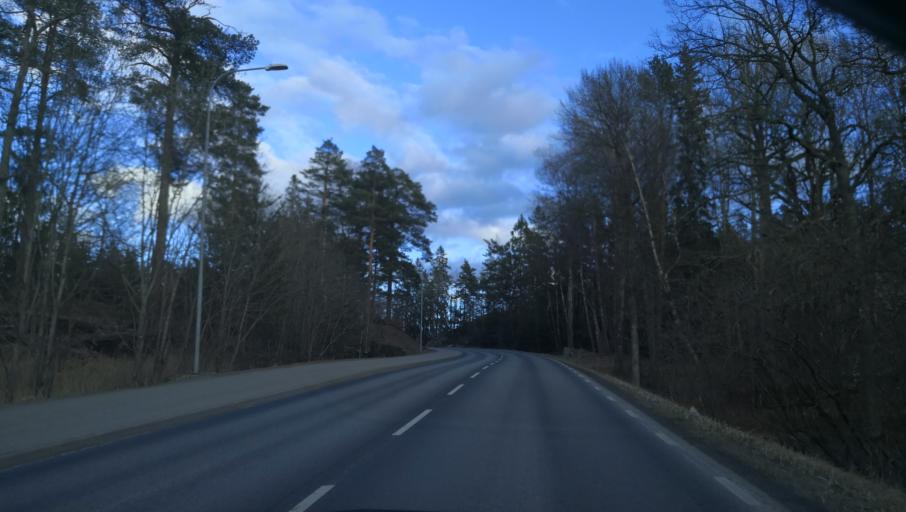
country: SE
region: Stockholm
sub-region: Nacka Kommun
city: Boo
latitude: 59.3324
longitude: 18.3184
